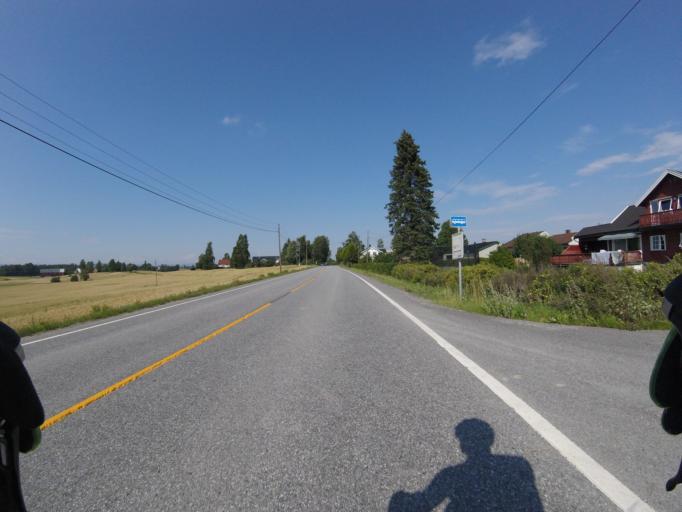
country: NO
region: Akershus
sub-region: Sorum
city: Frogner
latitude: 60.0455
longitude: 11.1182
